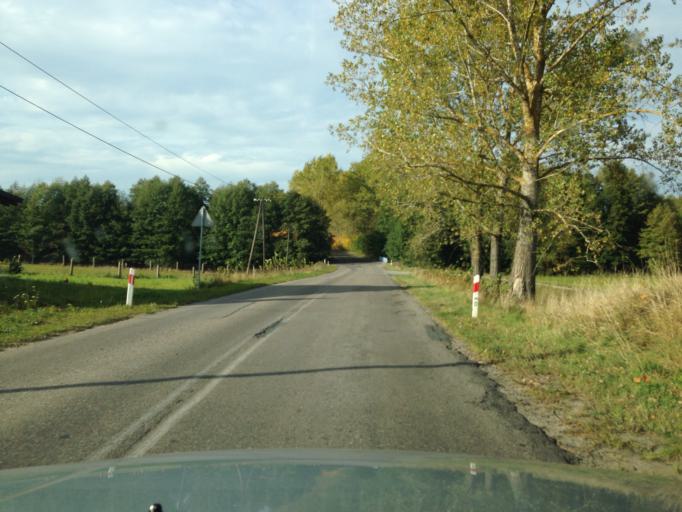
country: PL
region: Pomeranian Voivodeship
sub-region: Powiat koscierski
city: Koscierzyna
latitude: 54.0575
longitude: 18.0309
